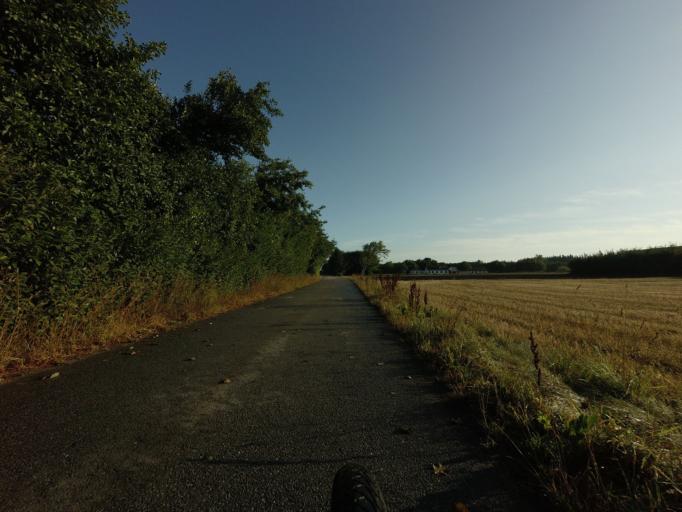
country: DK
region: North Denmark
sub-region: Hjorring Kommune
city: Vra
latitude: 57.3613
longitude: 9.8659
